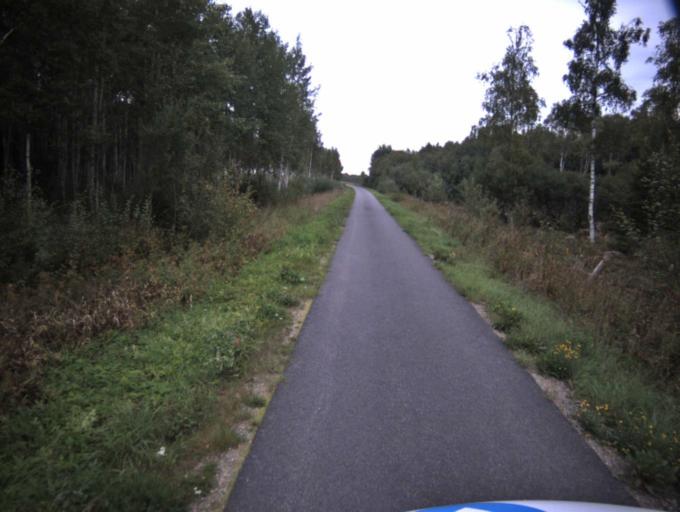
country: SE
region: Vaestra Goetaland
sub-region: Falkopings Kommun
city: Falkoeping
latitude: 57.9910
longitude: 13.5371
